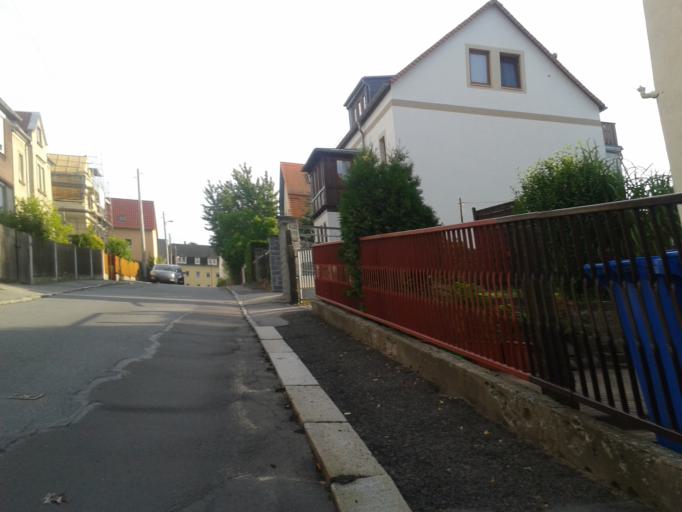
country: DE
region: Saxony
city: Albertstadt
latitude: 51.1104
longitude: 13.7718
